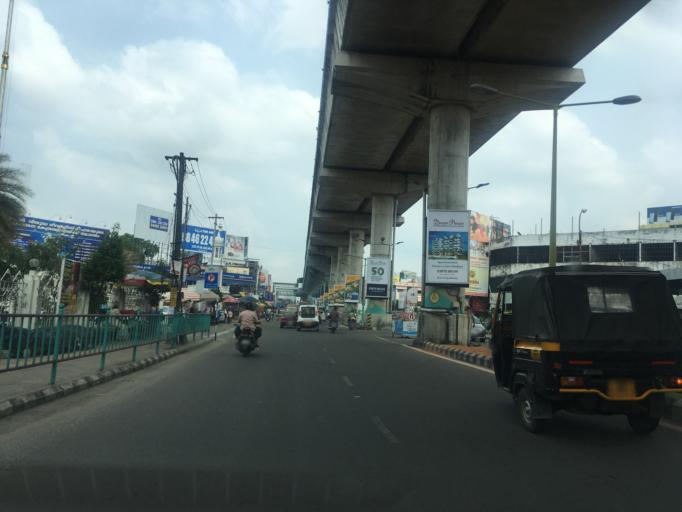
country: IN
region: Kerala
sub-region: Ernakulam
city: Elur
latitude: 10.0215
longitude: 76.3062
